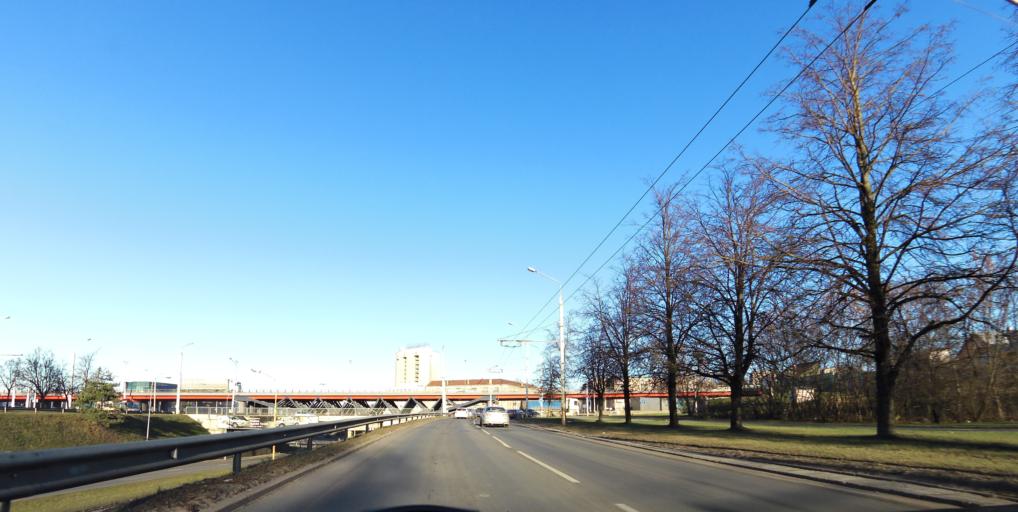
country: LT
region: Vilnius County
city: Vilkpede
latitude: 54.6672
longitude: 25.2378
